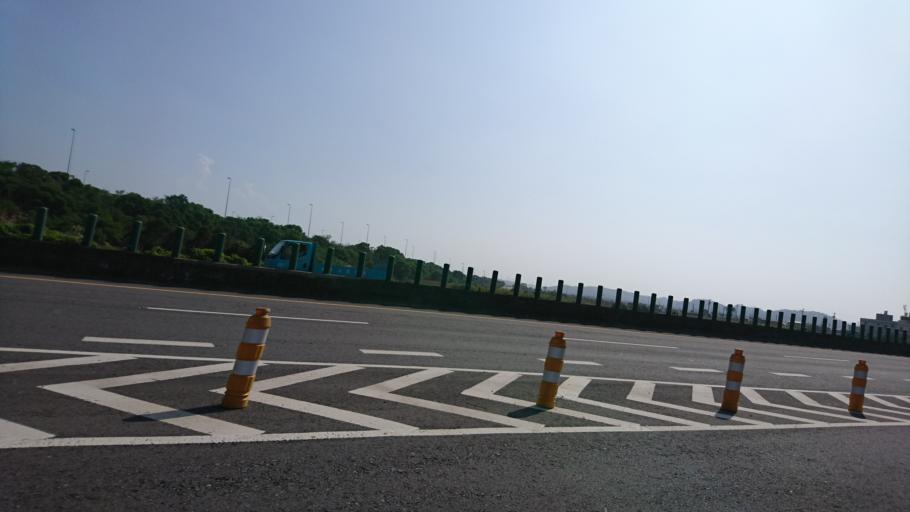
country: TW
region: Taiwan
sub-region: Miaoli
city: Miaoli
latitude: 24.6800
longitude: 120.8459
